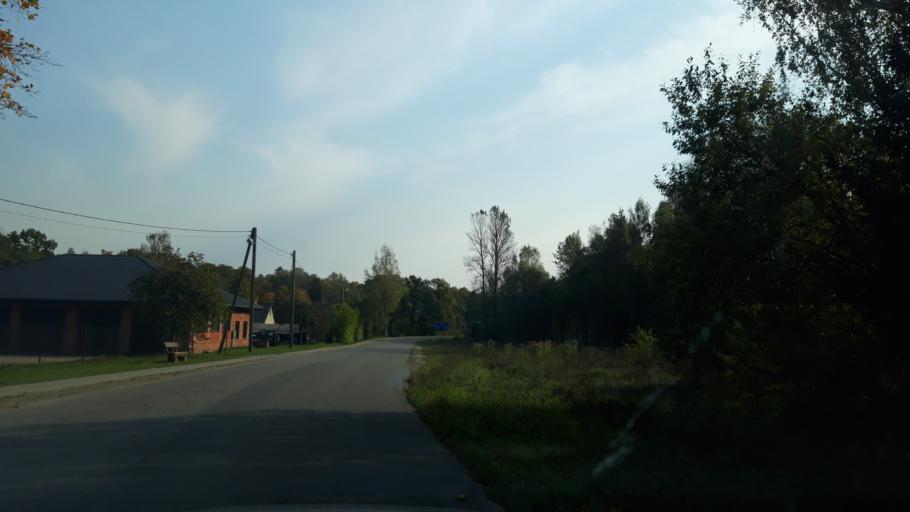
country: LV
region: Mazsalaca
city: Mazsalaca
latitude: 57.8585
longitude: 25.0479
